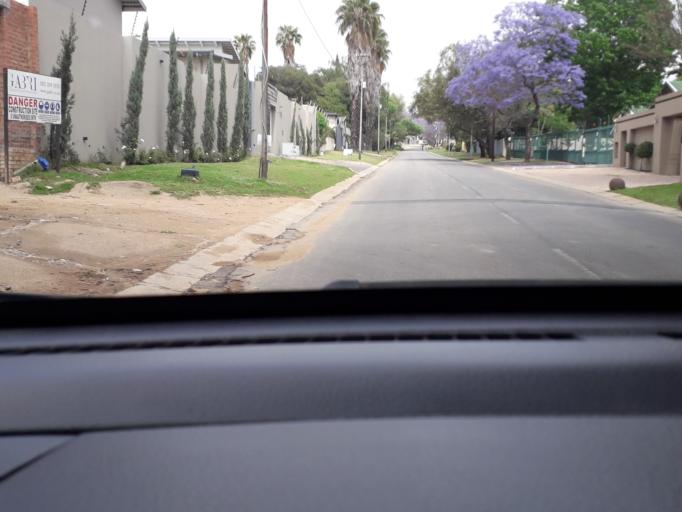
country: ZA
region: Gauteng
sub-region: City of Johannesburg Metropolitan Municipality
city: Modderfontein
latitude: -26.0927
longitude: 28.0631
